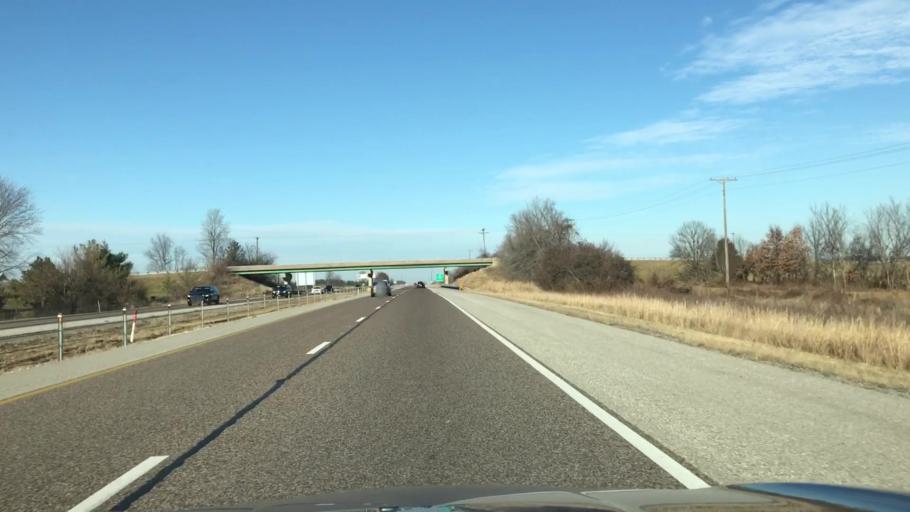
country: US
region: Illinois
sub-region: Madison County
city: Troy
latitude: 38.7809
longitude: -89.8992
